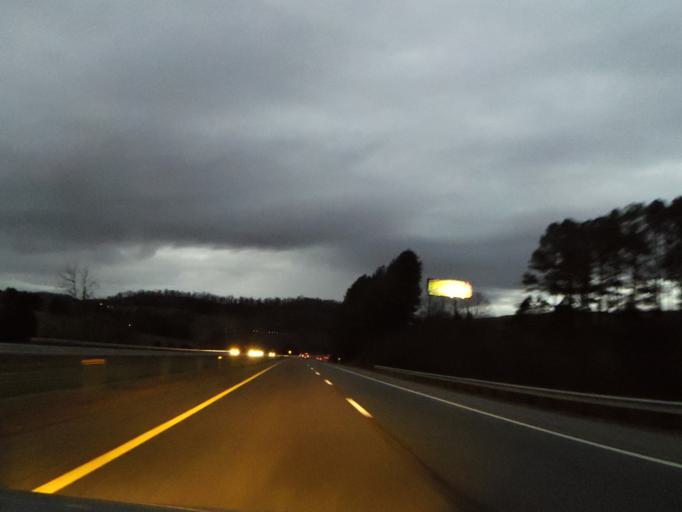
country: US
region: Tennessee
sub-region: Washington County
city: Gray
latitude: 36.4197
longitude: -82.4990
